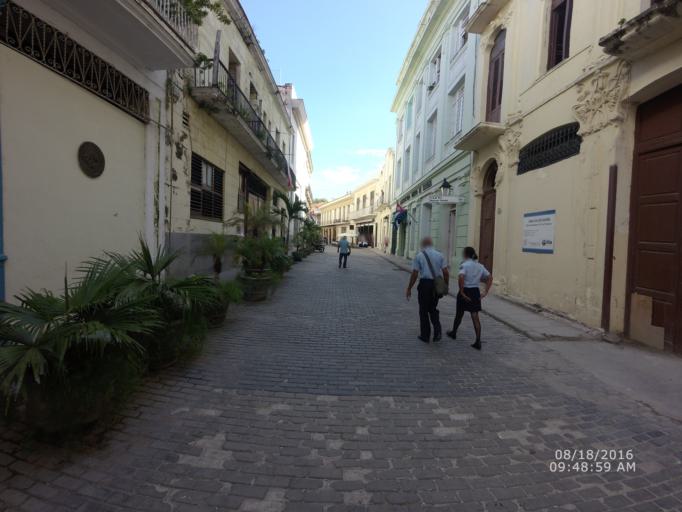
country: CU
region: La Habana
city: La Habana Vieja
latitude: 23.1368
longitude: -82.3497
